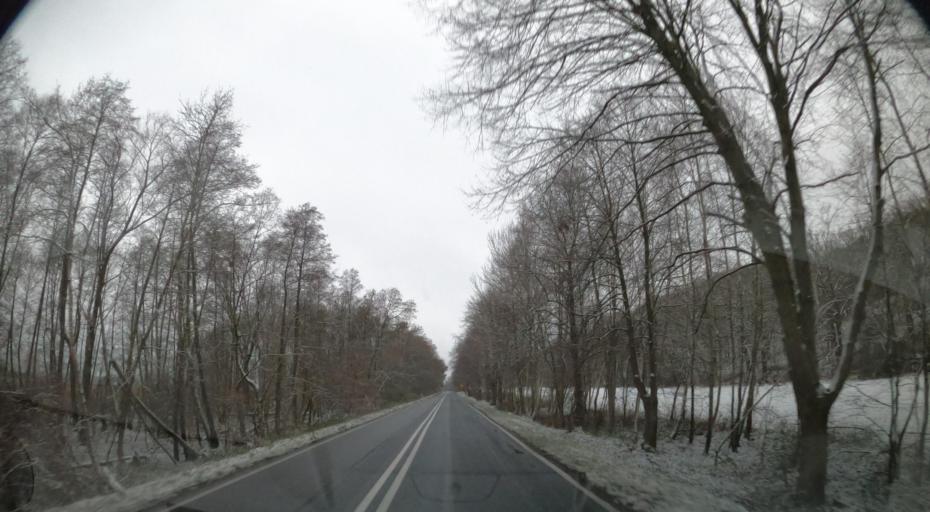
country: PL
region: Masovian Voivodeship
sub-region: Powiat plocki
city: Nowy Duninow
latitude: 52.5775
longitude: 19.5460
